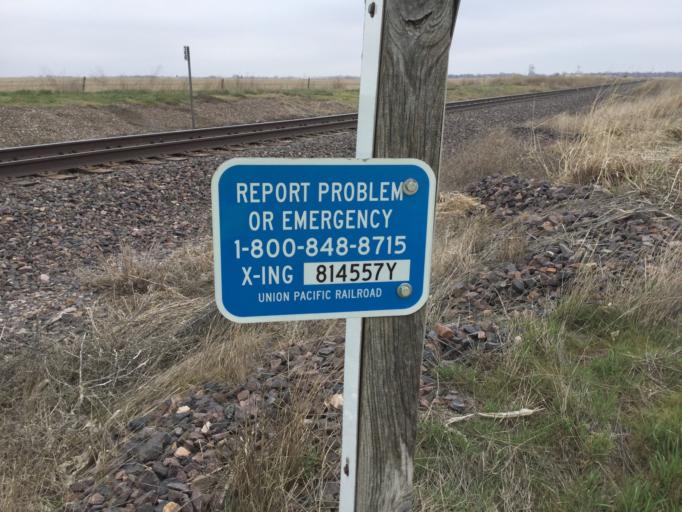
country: US
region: Kansas
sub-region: Russell County
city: Russell
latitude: 38.8530
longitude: -98.6136
